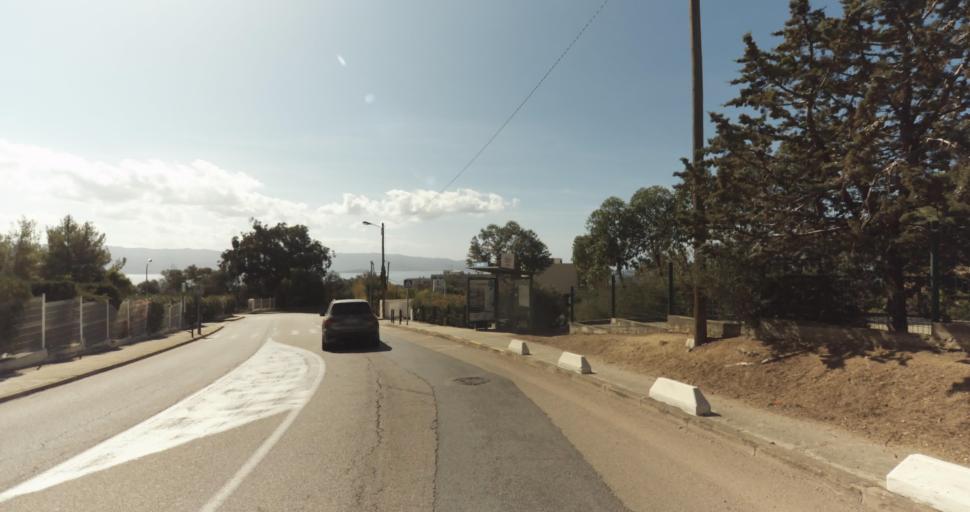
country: FR
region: Corsica
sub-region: Departement de la Corse-du-Sud
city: Ajaccio
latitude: 41.9214
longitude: 8.7298
